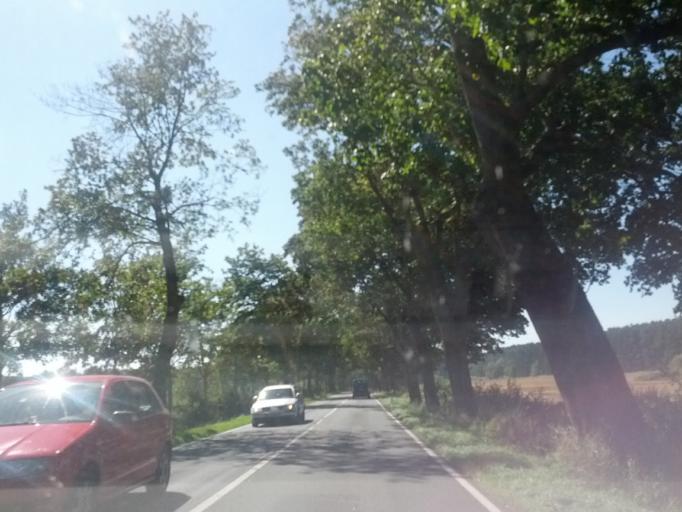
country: DE
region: Mecklenburg-Vorpommern
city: Bergen auf Ruegen
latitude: 54.4466
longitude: 13.4384
